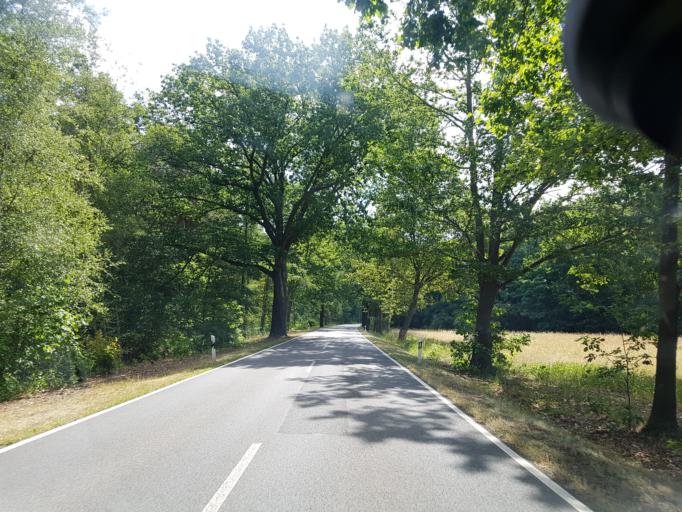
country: DE
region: Brandenburg
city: Neupetershain
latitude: 51.6837
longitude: 14.1461
